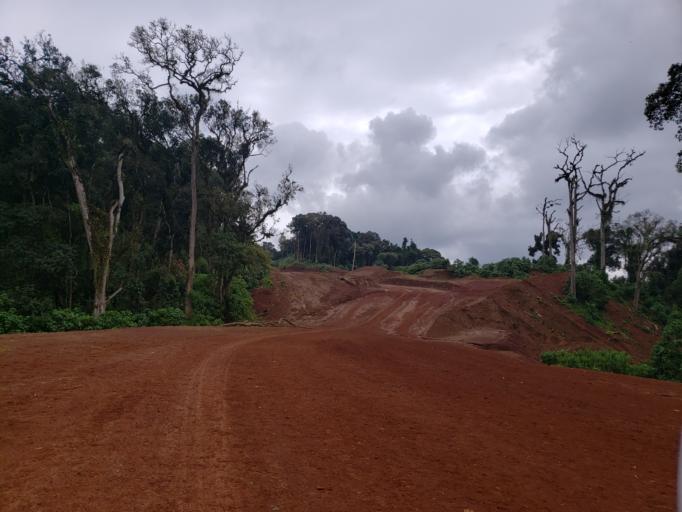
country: ET
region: Oromiya
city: Dodola
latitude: 6.5800
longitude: 39.4189
